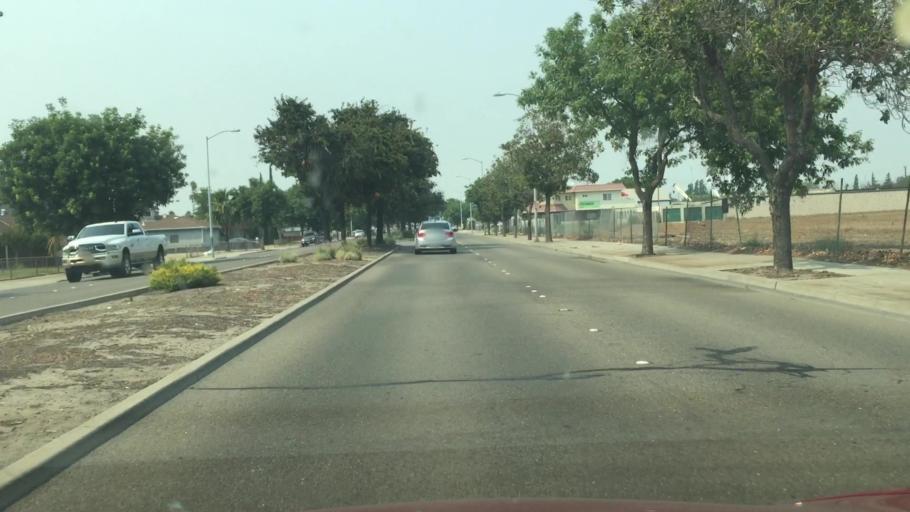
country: US
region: California
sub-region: San Joaquin County
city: Manteca
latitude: 37.7901
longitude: -121.2160
